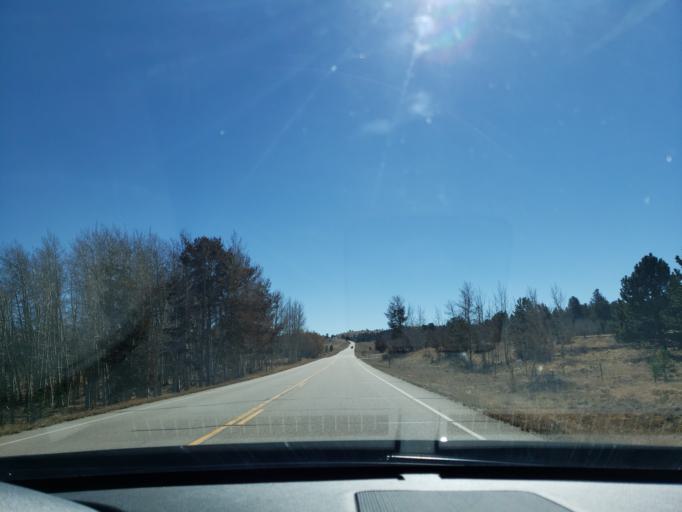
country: US
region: Colorado
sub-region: Chaffee County
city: Buena Vista
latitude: 38.9062
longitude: -105.6983
